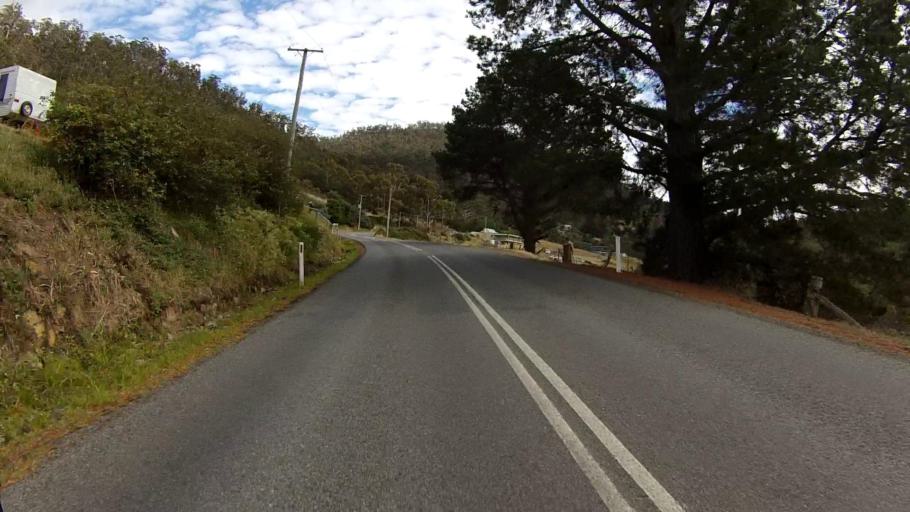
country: AU
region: Tasmania
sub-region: Clarence
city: Lindisfarne
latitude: -42.7890
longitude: 147.3604
